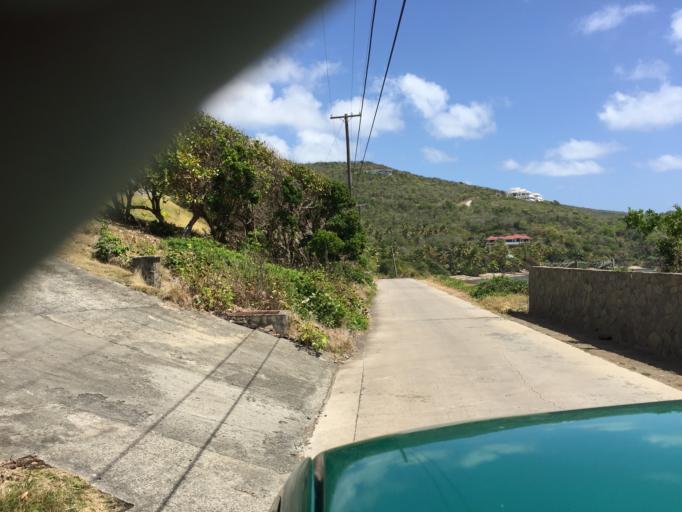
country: VC
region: Grenadines
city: Port Elizabeth
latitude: 13.0226
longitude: -61.2190
